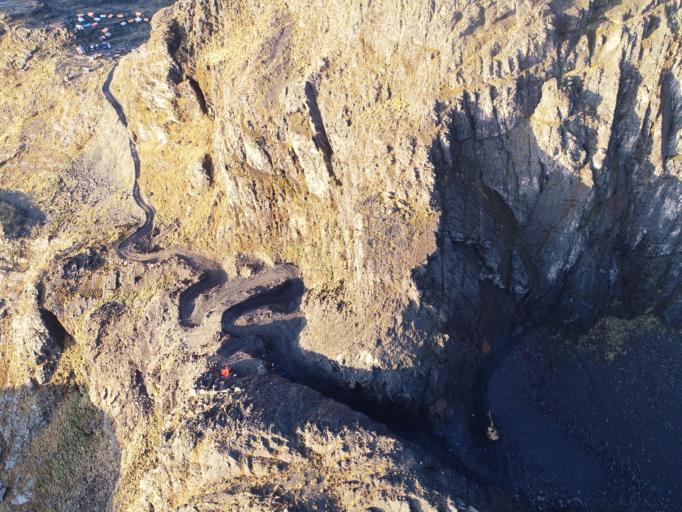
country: PE
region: Puno
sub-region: San Antonio De Putina
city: Sina
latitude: -14.7359
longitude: -69.0501
